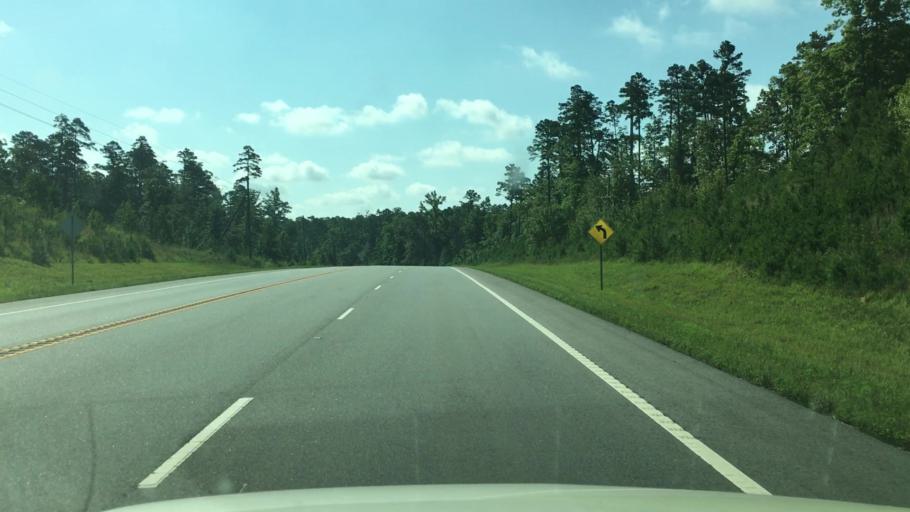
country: US
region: Arkansas
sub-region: Garland County
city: Rockwell
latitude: 34.5205
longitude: -93.3161
